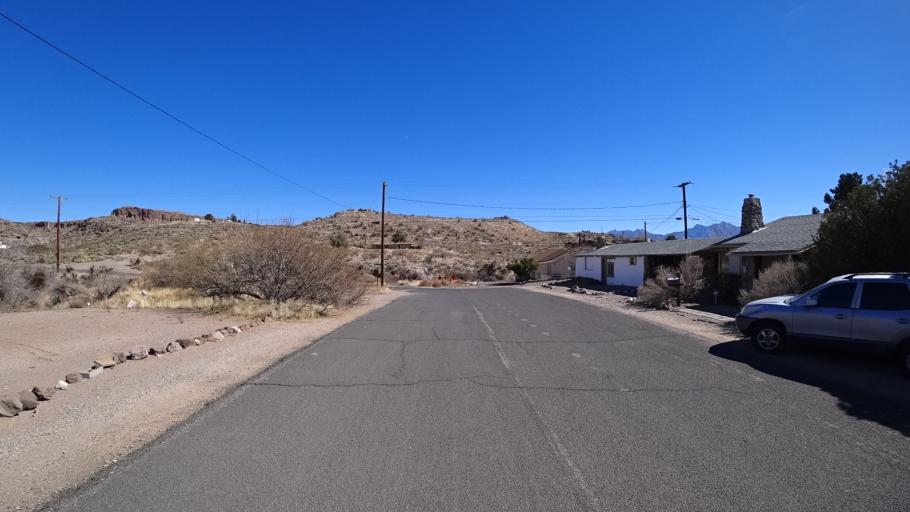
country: US
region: Arizona
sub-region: Mohave County
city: Kingman
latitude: 35.1976
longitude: -114.0610
